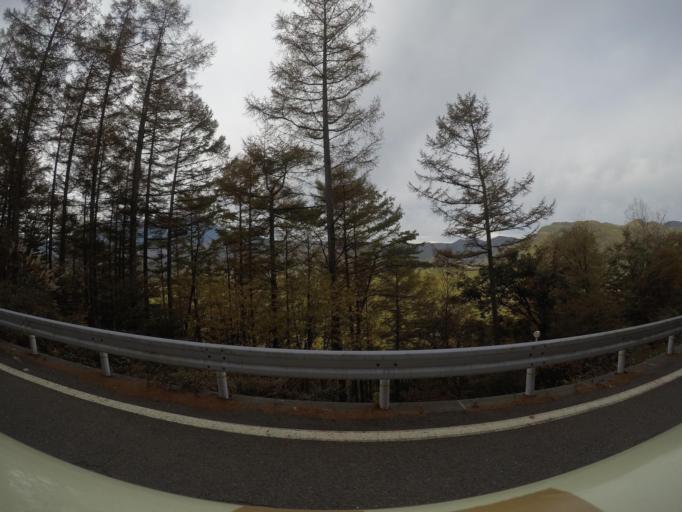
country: JP
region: Gifu
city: Takayama
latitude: 35.9404
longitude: 137.5809
